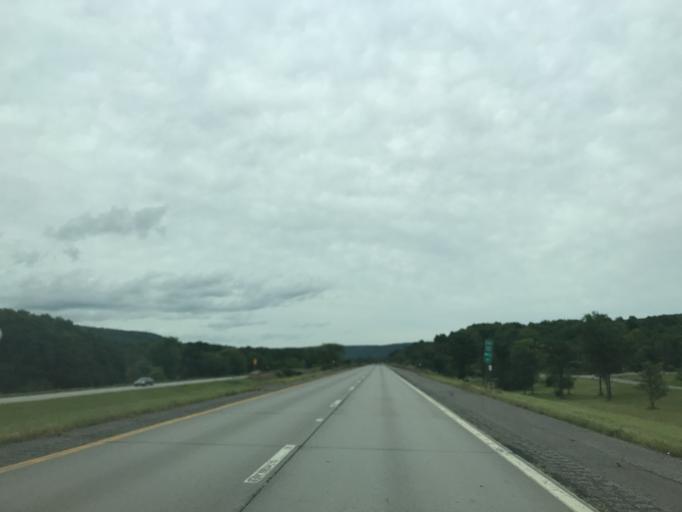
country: US
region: New York
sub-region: Otsego County
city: Oneonta
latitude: 42.4812
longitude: -74.9720
